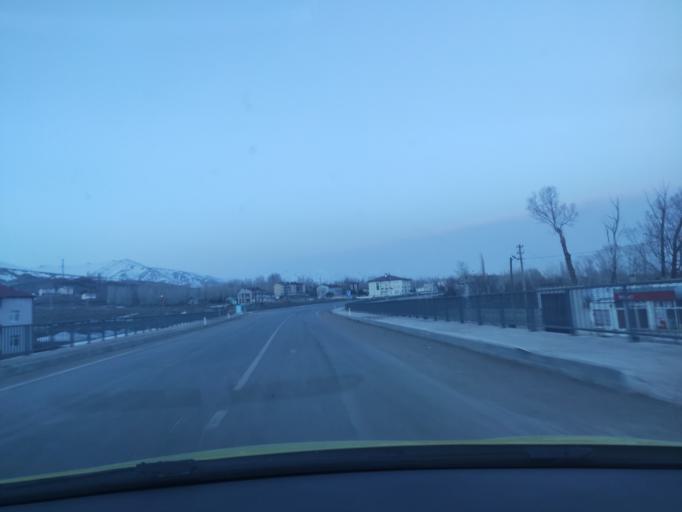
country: TR
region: Bayburt
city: Aydintepe
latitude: 40.3863
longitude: 40.1361
